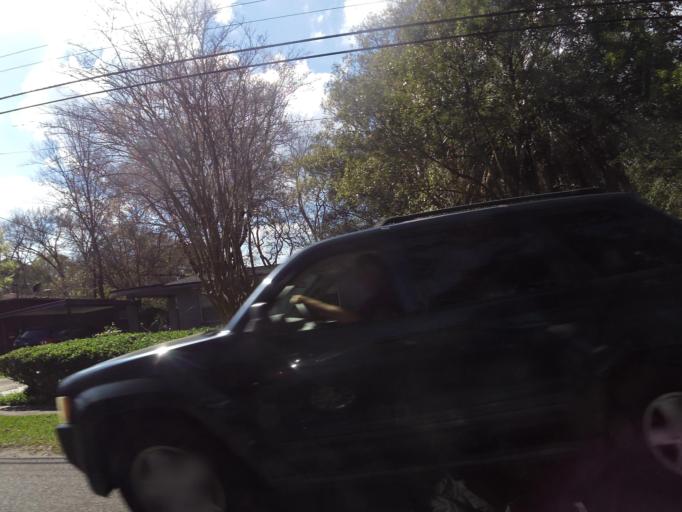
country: US
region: Florida
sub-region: Duval County
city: Jacksonville
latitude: 30.3387
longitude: -81.7184
